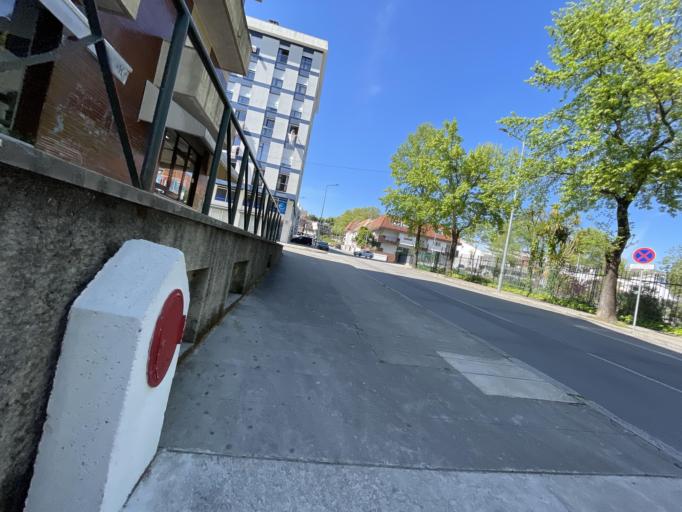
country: PT
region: Braga
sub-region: Guimaraes
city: Guimaraes
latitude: 41.4452
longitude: -8.2844
